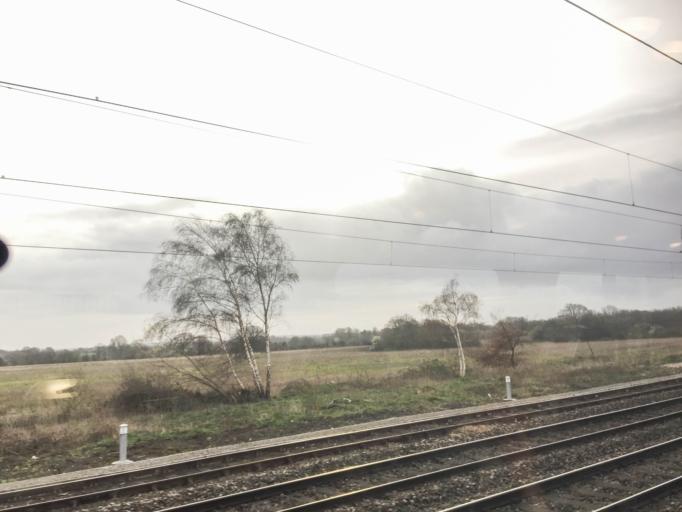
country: GB
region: England
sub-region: Cheshire East
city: Weston
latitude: 53.0738
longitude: -2.4238
